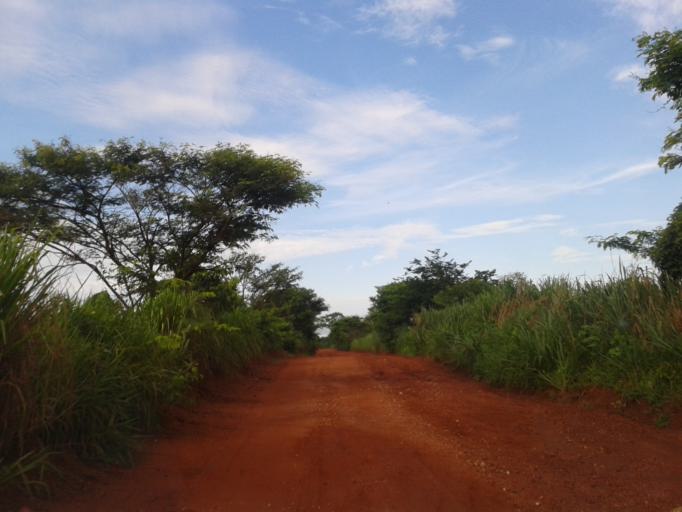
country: BR
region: Minas Gerais
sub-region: Santa Vitoria
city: Santa Vitoria
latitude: -19.1132
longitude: -50.5230
